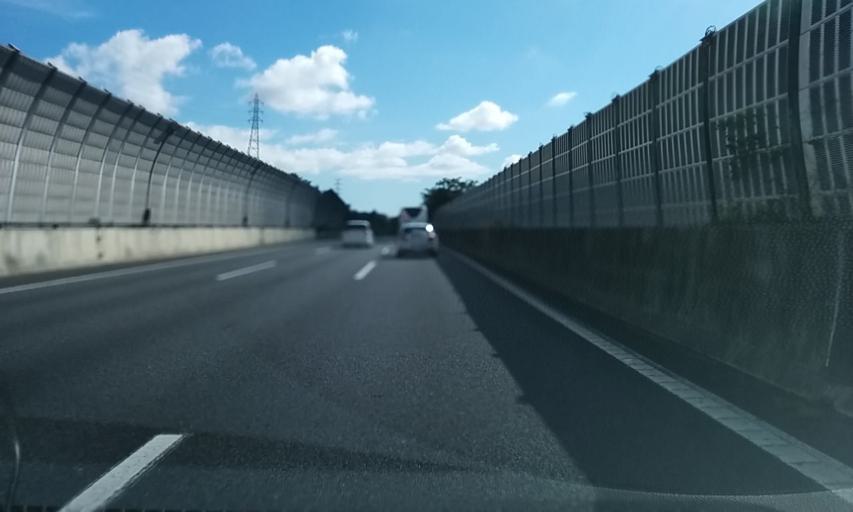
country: JP
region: Hyogo
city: Takarazuka
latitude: 34.8188
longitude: 135.3412
